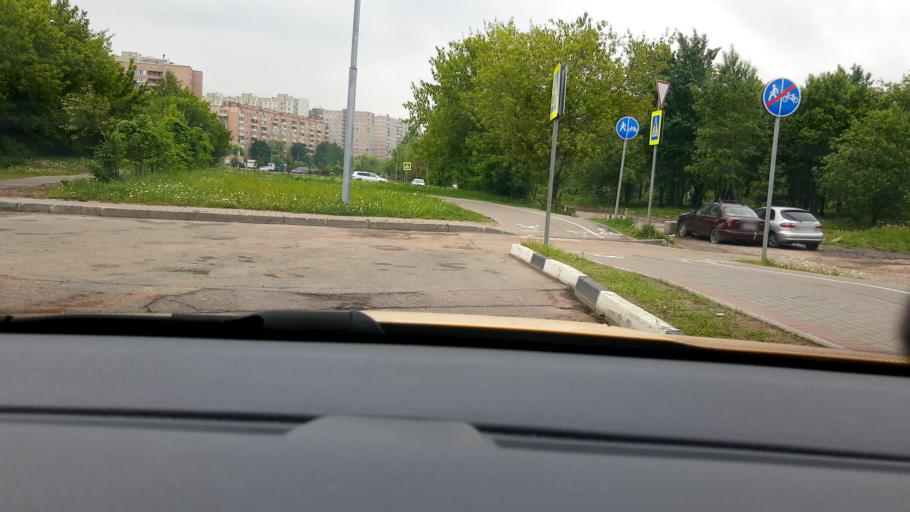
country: RU
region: Moscow
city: Yaroslavskiy
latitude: 55.8991
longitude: 37.7115
